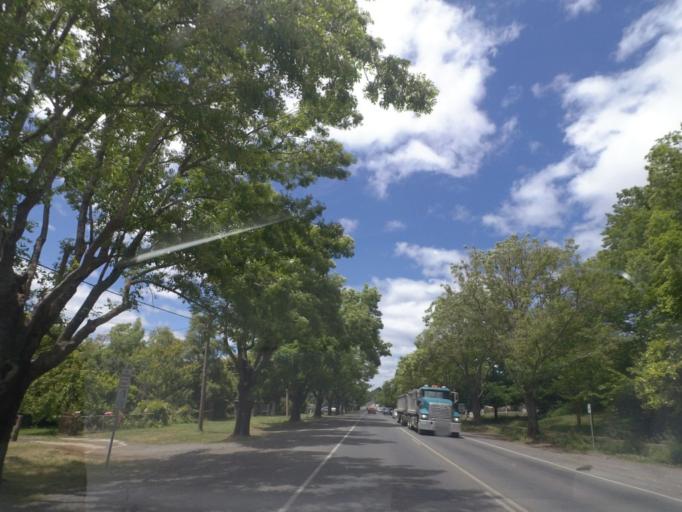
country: AU
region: Victoria
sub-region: Mount Alexander
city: Castlemaine
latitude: -37.3405
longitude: 144.1524
